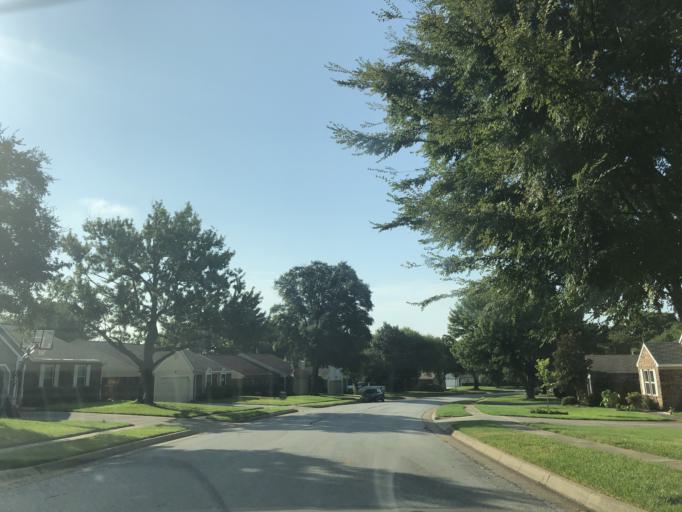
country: US
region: Texas
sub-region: Tarrant County
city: Euless
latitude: 32.8753
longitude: -97.0809
